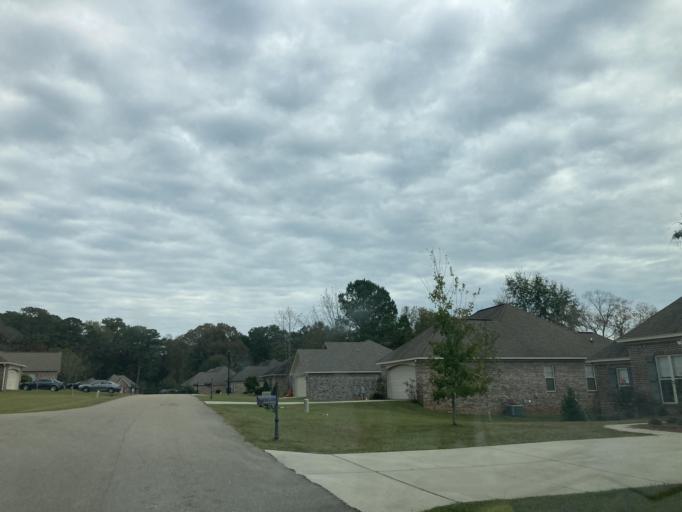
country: US
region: Mississippi
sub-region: Lamar County
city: West Hattiesburg
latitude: 31.2910
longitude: -89.4439
